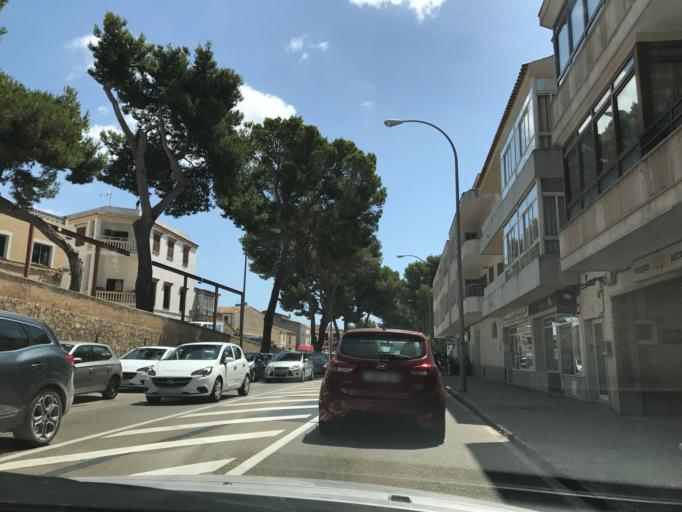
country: ES
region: Balearic Islands
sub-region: Illes Balears
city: Arta
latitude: 39.6909
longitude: 3.3507
